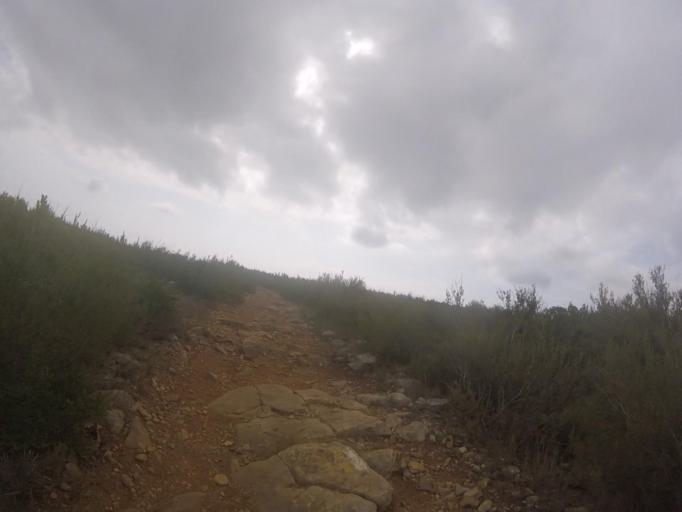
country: ES
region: Valencia
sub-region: Provincia de Castello
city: Santa Magdalena de Pulpis
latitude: 40.3482
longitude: 0.3428
